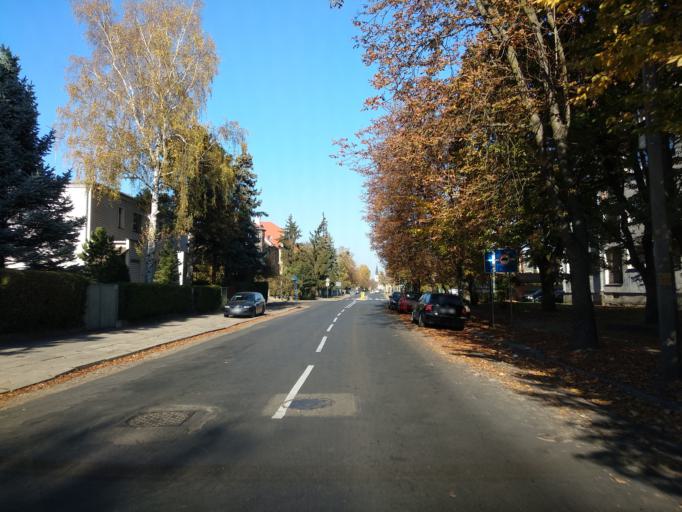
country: PL
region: Lower Silesian Voivodeship
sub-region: Powiat wroclawski
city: Wroclaw
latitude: 51.0832
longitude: 17.0028
